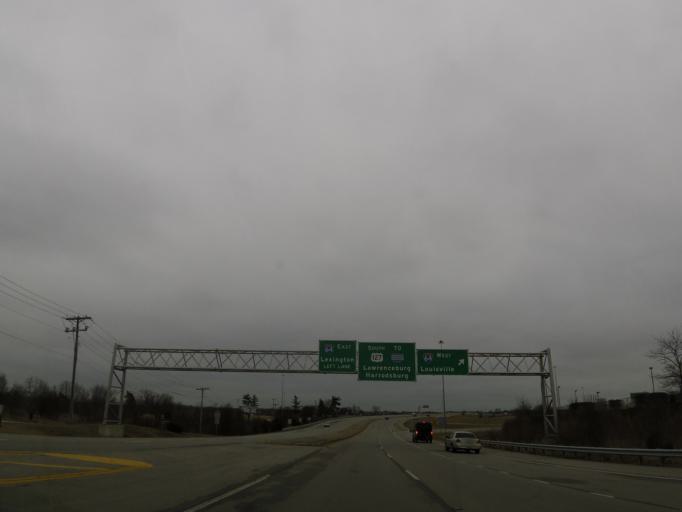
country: US
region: Kentucky
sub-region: Franklin County
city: Frankfort
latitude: 38.1630
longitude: -84.8957
